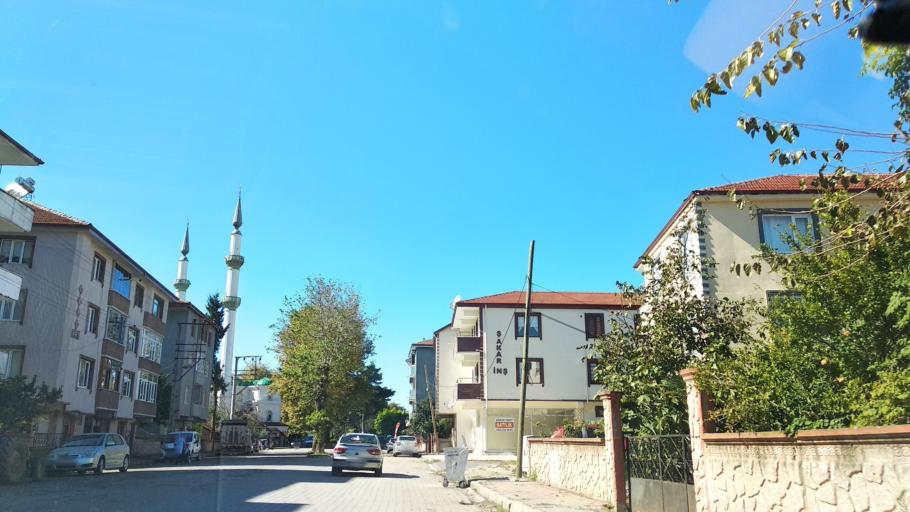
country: TR
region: Sakarya
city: Karasu
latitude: 41.0907
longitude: 30.7023
